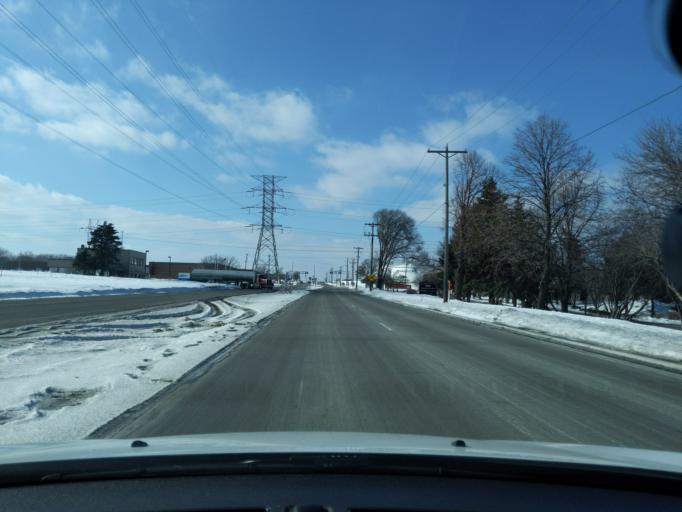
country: US
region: Minnesota
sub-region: Hennepin County
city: Saint Anthony
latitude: 45.0206
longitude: -93.1945
